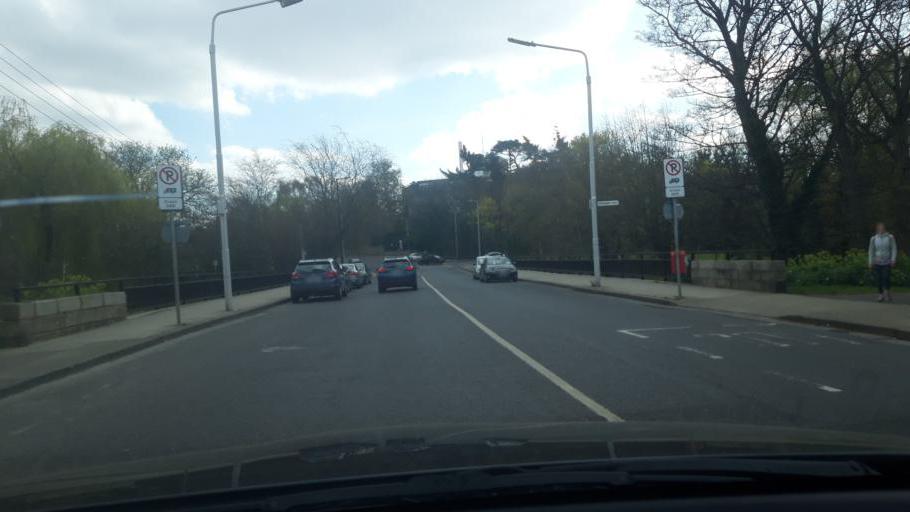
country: IE
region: Leinster
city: Rathgar
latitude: 53.3062
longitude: -6.2672
